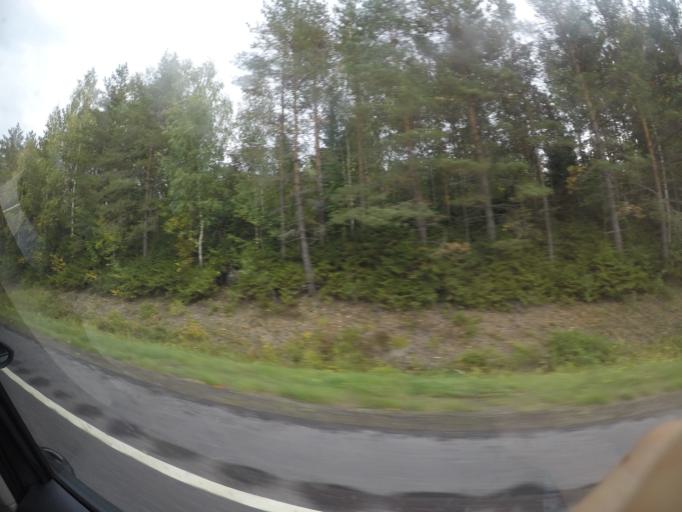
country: FI
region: Haeme
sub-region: Haemeenlinna
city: Parola
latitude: 61.1024
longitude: 24.4081
